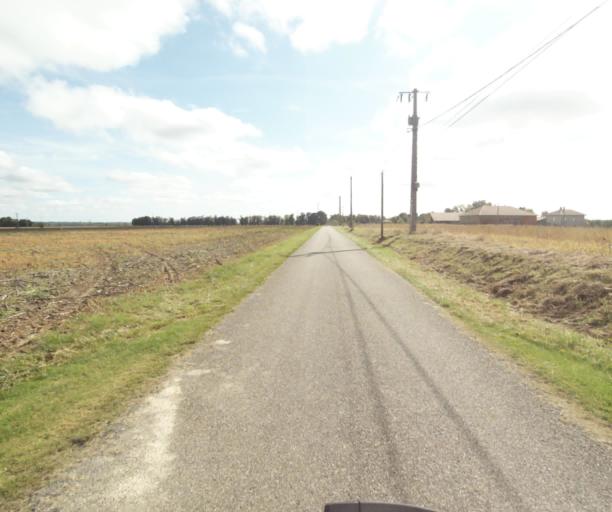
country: FR
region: Midi-Pyrenees
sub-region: Departement du Tarn-et-Garonne
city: Finhan
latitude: 43.9327
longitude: 1.2152
